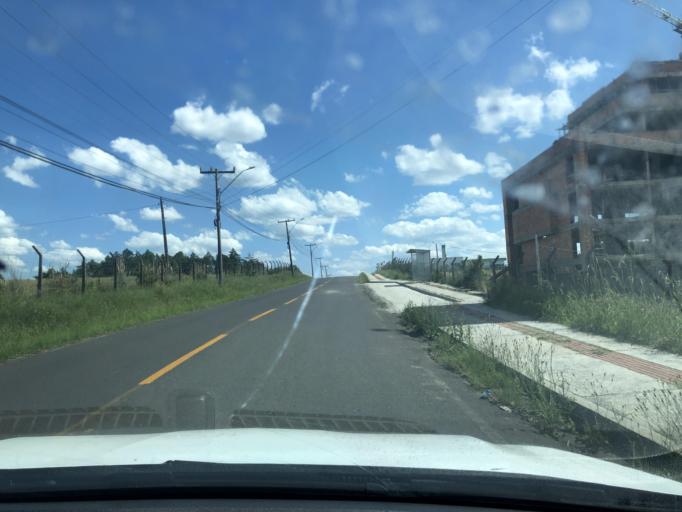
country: BR
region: Santa Catarina
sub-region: Lages
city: Lages
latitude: -27.8017
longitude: -50.3367
